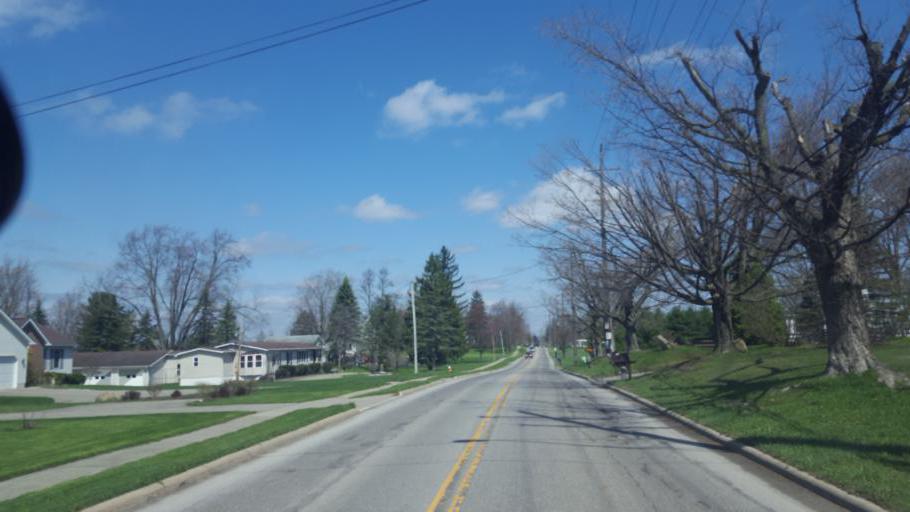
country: US
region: Ohio
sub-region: Geauga County
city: Middlefield
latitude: 41.4542
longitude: -81.0808
